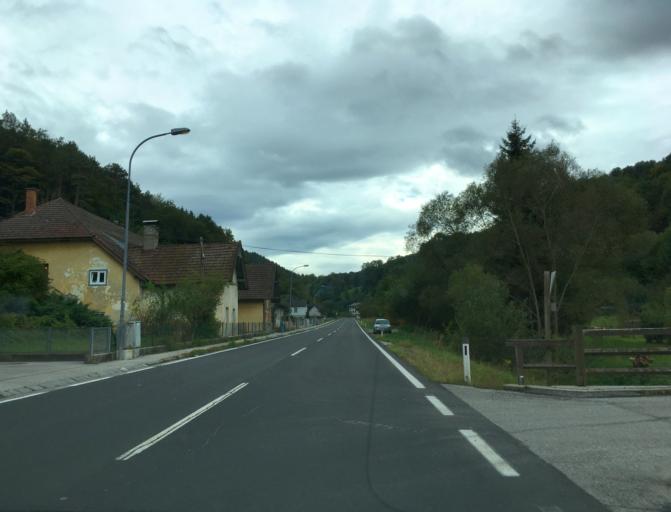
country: AT
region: Lower Austria
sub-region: Politischer Bezirk Neunkirchen
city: Edlitz
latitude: 47.5877
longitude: 16.1468
